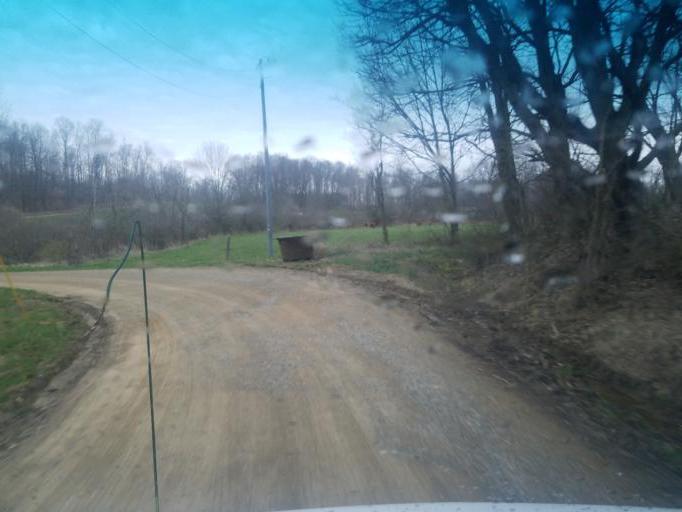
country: US
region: Ohio
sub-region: Knox County
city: Fredericktown
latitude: 40.5287
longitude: -82.4308
